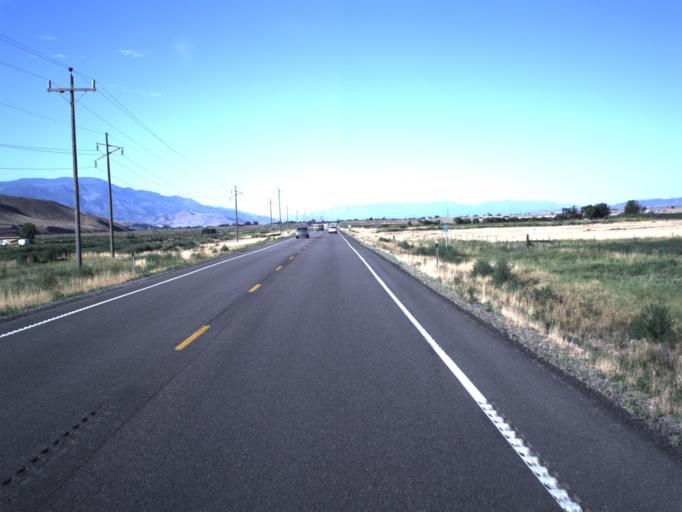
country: US
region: Utah
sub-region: Sevier County
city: Aurora
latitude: 38.8935
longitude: -111.9468
